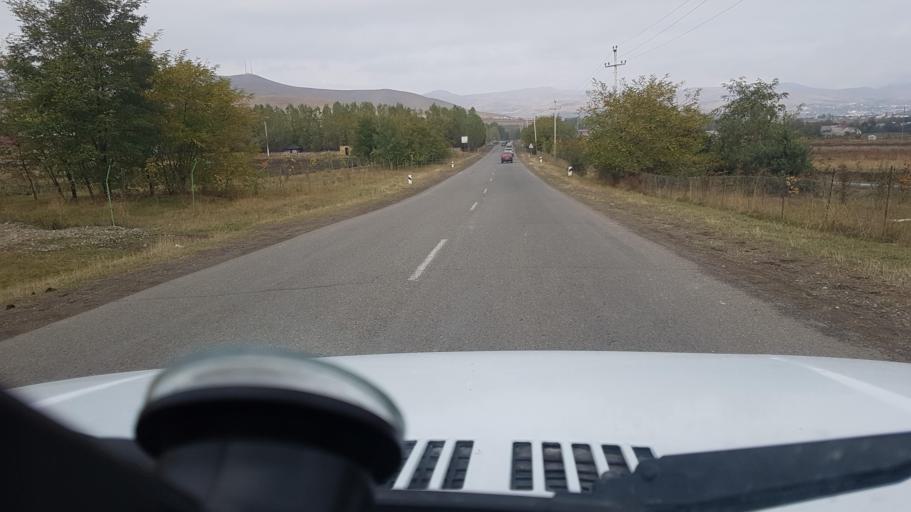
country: AZ
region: Gadabay Rayon
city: Ariqdam
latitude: 40.6272
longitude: 45.8157
